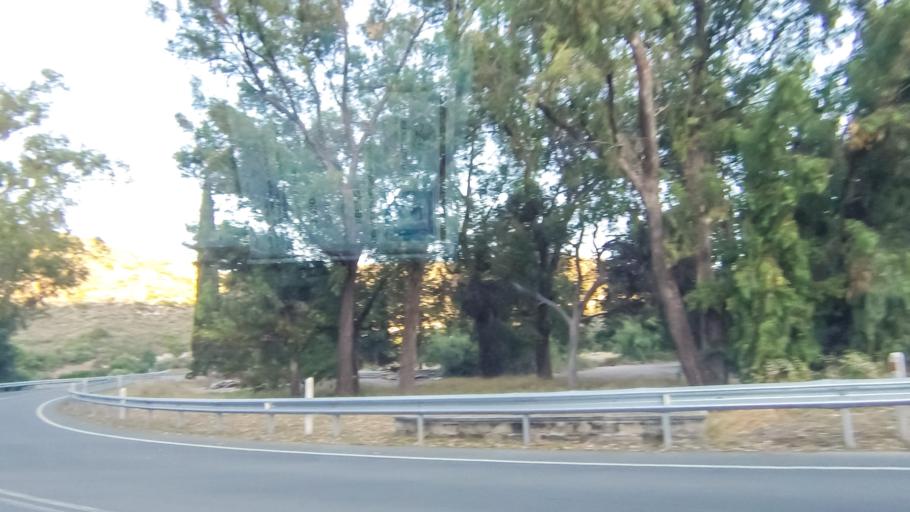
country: CY
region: Limassol
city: Sotira
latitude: 34.6765
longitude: 32.8212
